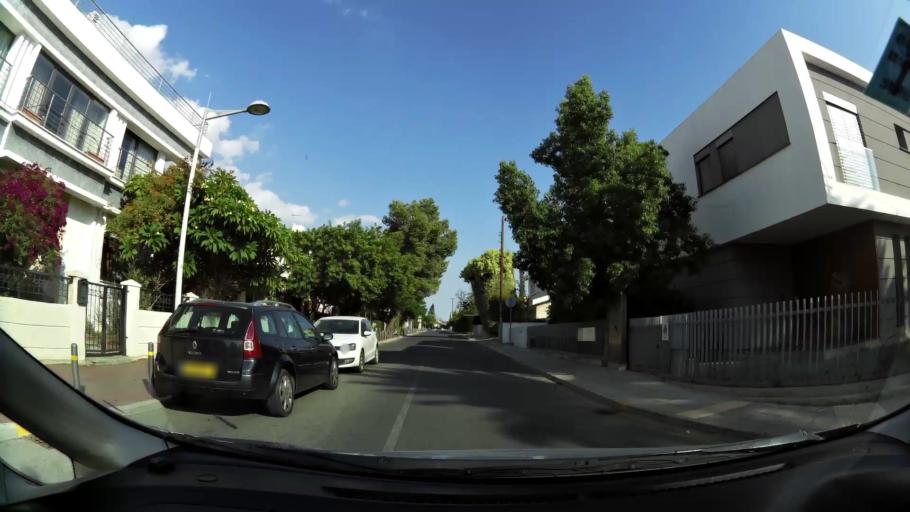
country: CY
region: Lefkosia
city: Nicosia
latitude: 35.1774
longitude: 33.3424
